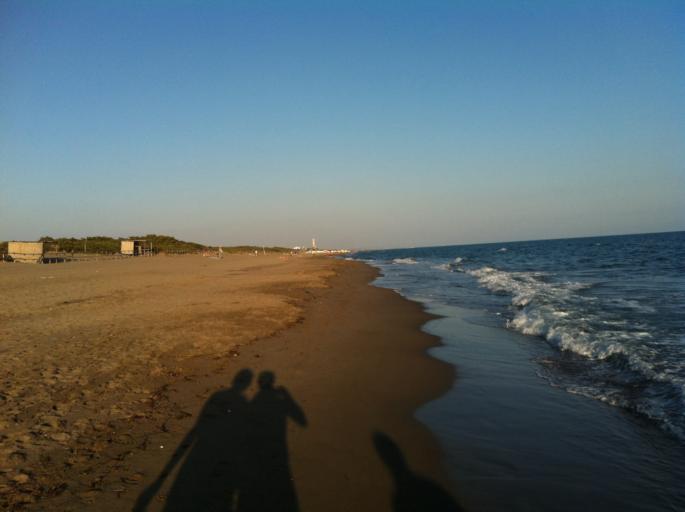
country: IT
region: Latium
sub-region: Provincia di Viterbo
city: Pescia Romana
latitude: 42.3812
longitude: 11.4378
